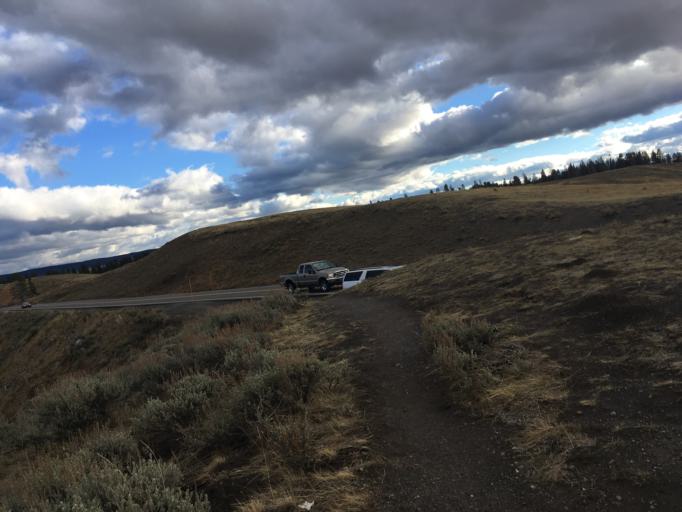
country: US
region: Montana
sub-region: Gallatin County
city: West Yellowstone
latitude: 44.6702
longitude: -110.4715
